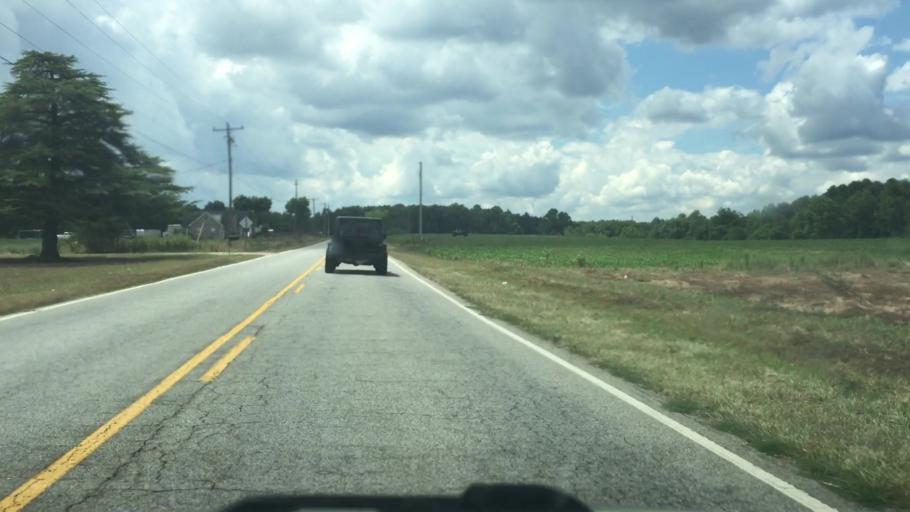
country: US
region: North Carolina
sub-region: Rowan County
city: Enochville
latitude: 35.5860
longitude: -80.6529
